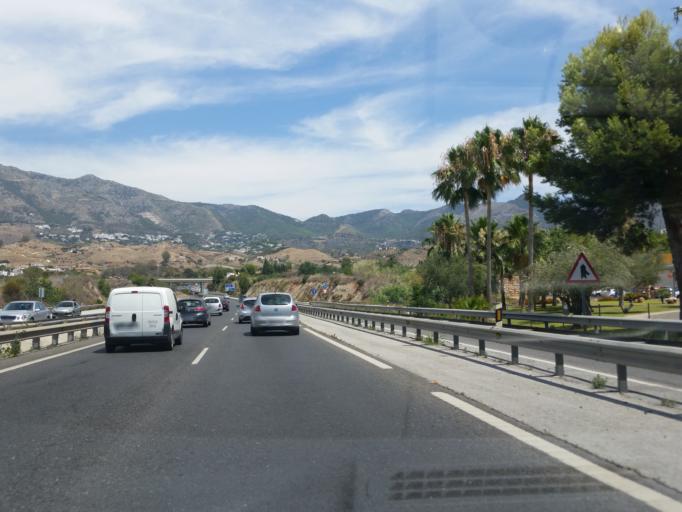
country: ES
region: Andalusia
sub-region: Provincia de Malaga
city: Fuengirola
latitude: 36.5636
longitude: -4.6217
